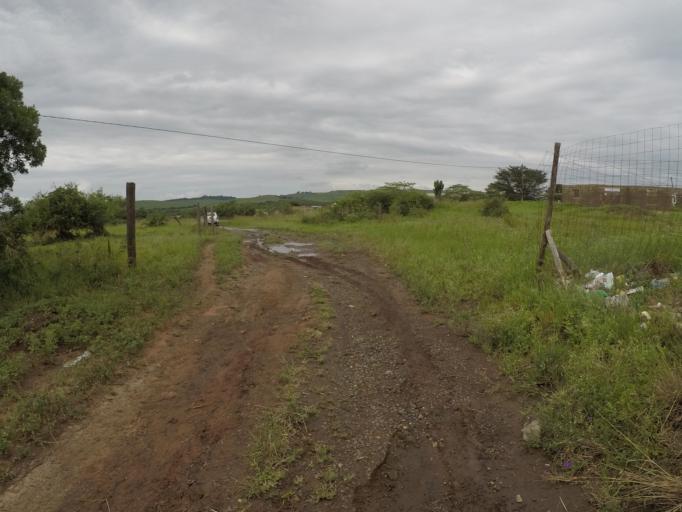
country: ZA
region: KwaZulu-Natal
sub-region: uThungulu District Municipality
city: Empangeni
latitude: -28.7141
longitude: 31.8627
